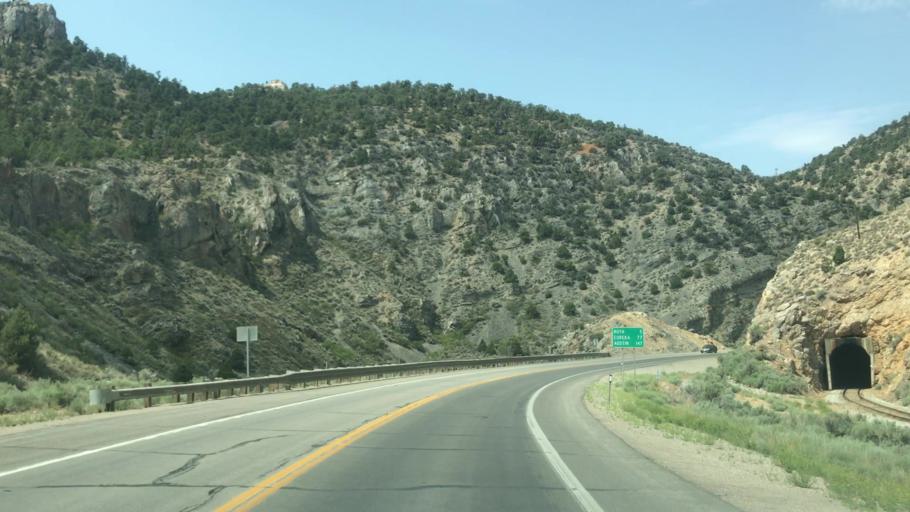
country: US
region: Nevada
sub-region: White Pine County
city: Ely
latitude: 39.2467
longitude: -114.9029
